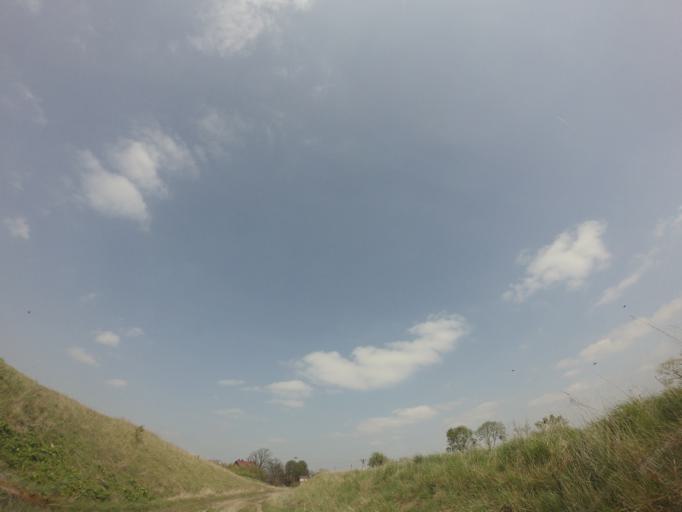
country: PL
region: West Pomeranian Voivodeship
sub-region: Powiat choszczenski
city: Pelczyce
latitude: 53.1016
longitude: 15.3330
